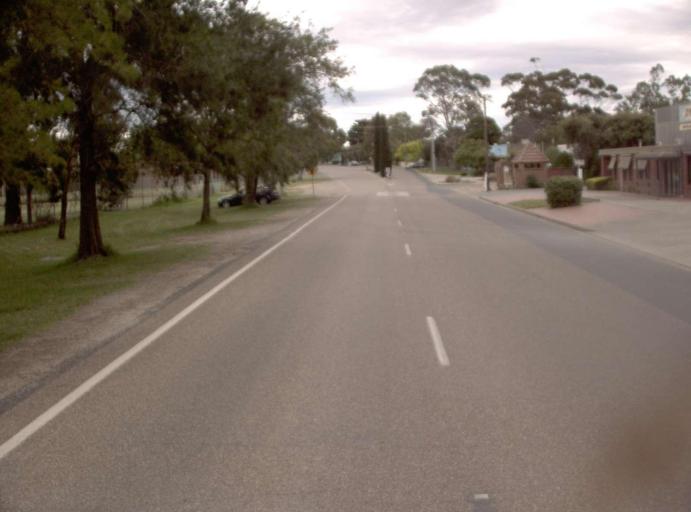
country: AU
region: Victoria
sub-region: Wellington
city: Sale
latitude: -38.1152
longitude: 147.0683
